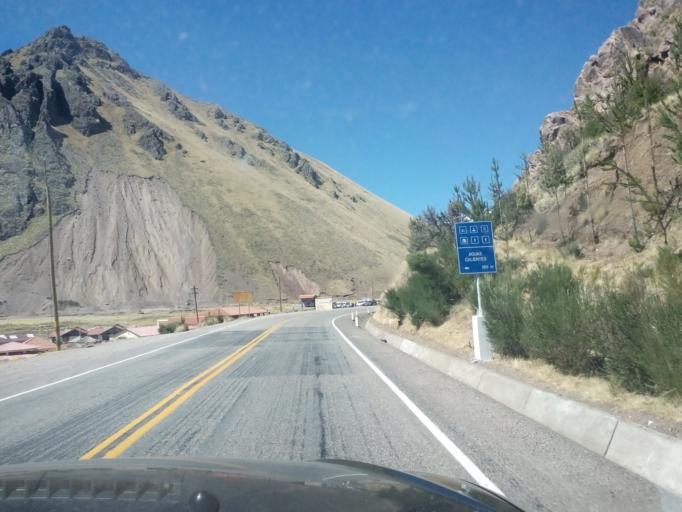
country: PE
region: Cusco
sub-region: Provincia de Canas
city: Layo
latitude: -14.4508
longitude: -71.0746
